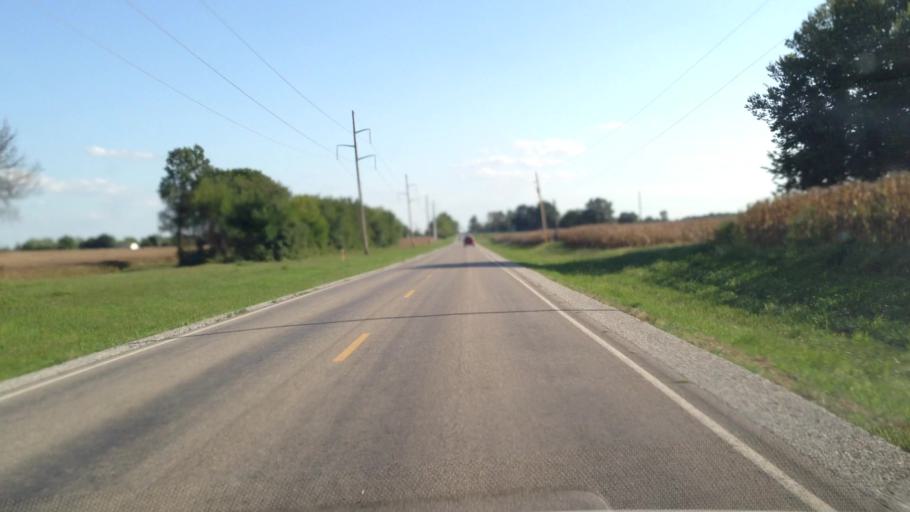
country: US
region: Kansas
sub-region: Crawford County
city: Pittsburg
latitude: 37.3715
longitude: -94.6314
